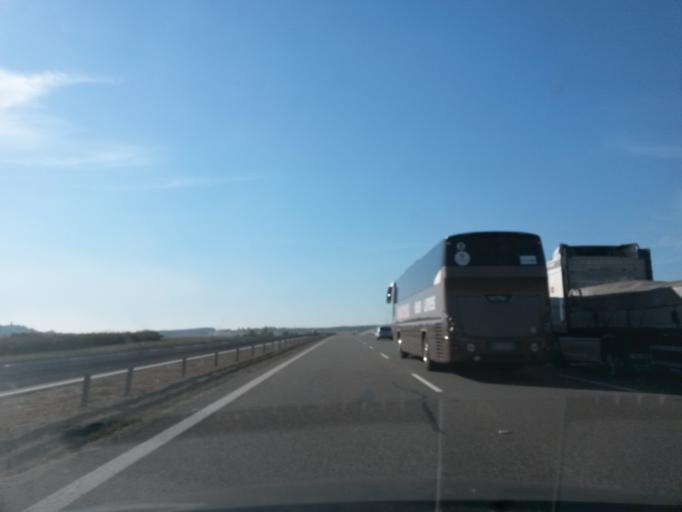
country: PL
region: Opole Voivodeship
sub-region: Powiat strzelecki
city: Lesnica
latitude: 50.4665
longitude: 18.1994
